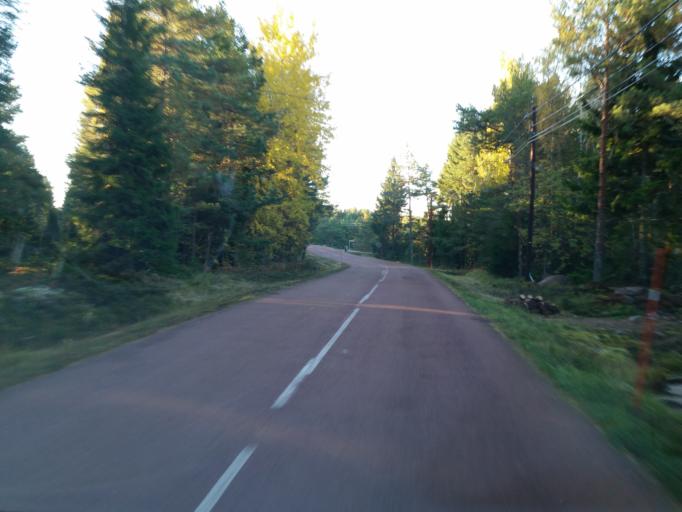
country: AX
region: Alands skaergard
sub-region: Vardoe
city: Vardoe
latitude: 60.3000
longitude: 20.3826
